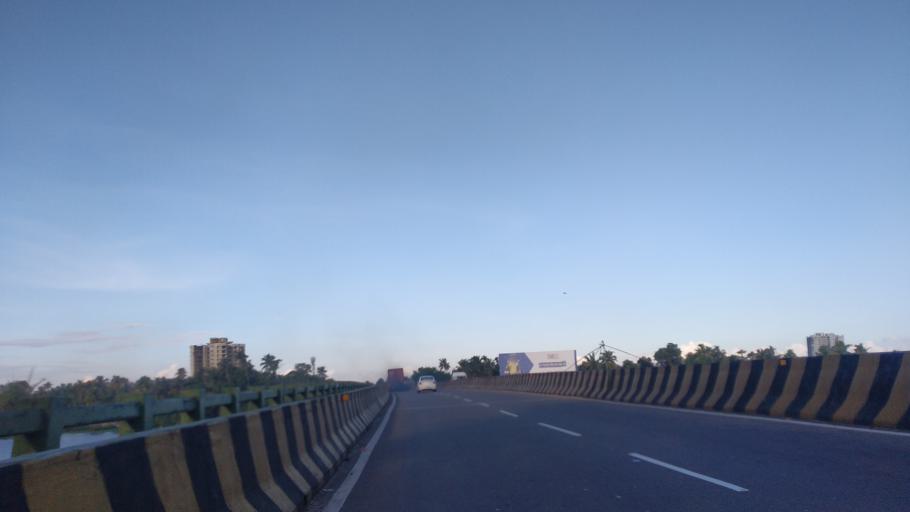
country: IN
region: Kerala
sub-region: Ernakulam
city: Elur
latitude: 10.0515
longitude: 76.2787
